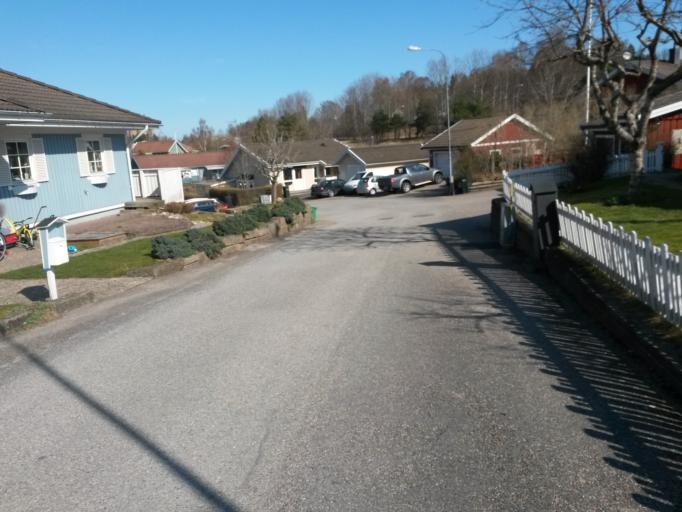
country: SE
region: Vaestra Goetaland
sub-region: Vargarda Kommun
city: Vargarda
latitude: 58.0248
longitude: 12.7983
